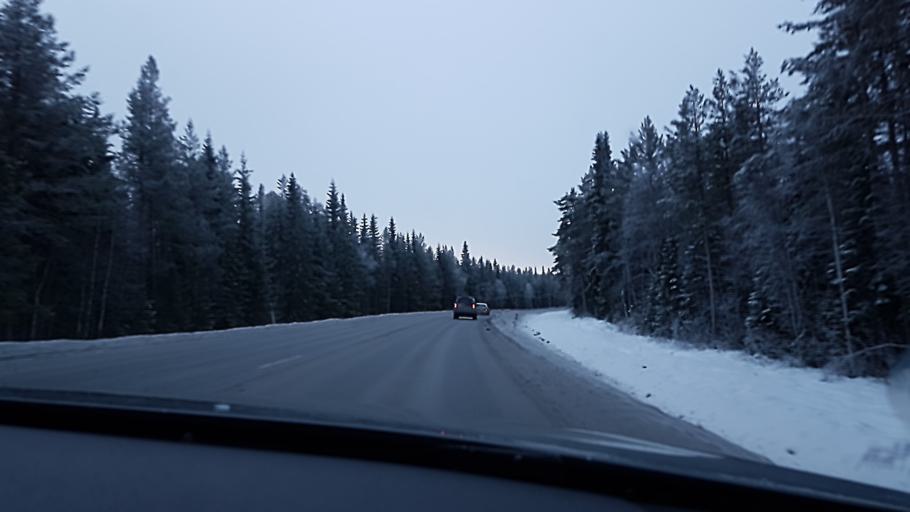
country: SE
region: Jaemtland
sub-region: OEstersunds Kommun
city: Lit
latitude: 63.2700
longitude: 14.8568
